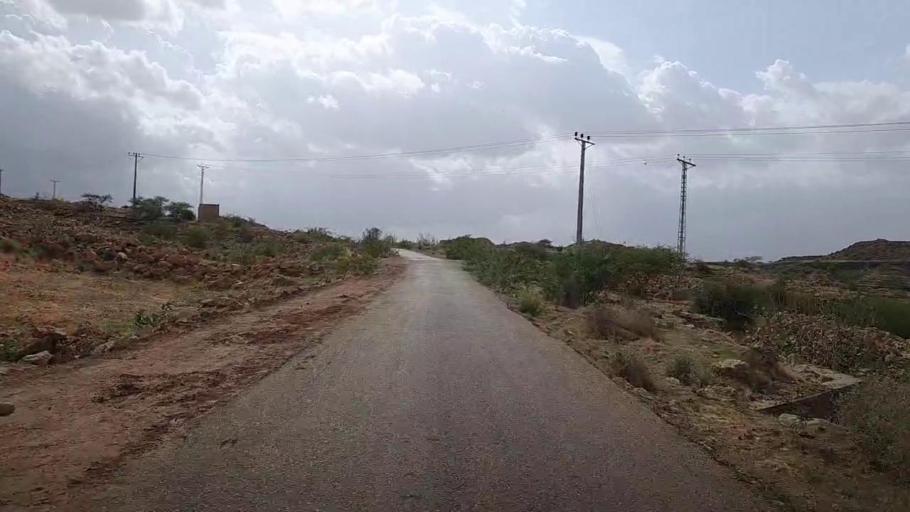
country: PK
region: Sindh
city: Jamshoro
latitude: 25.3966
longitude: 67.7401
